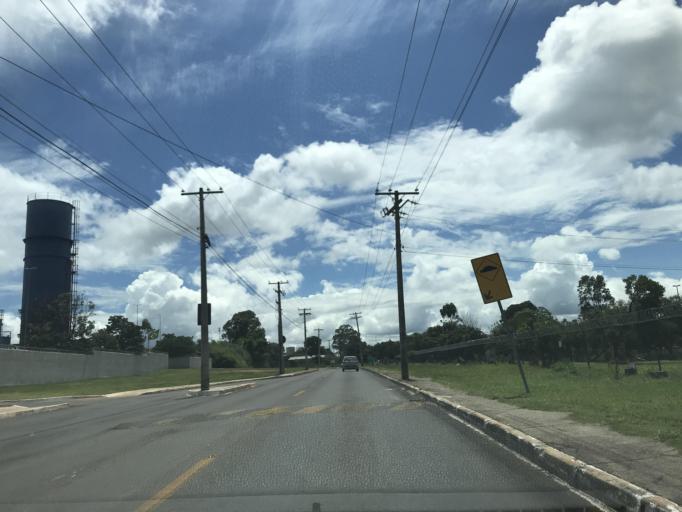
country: BR
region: Federal District
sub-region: Brasilia
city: Brasilia
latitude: -15.7329
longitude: -47.9004
